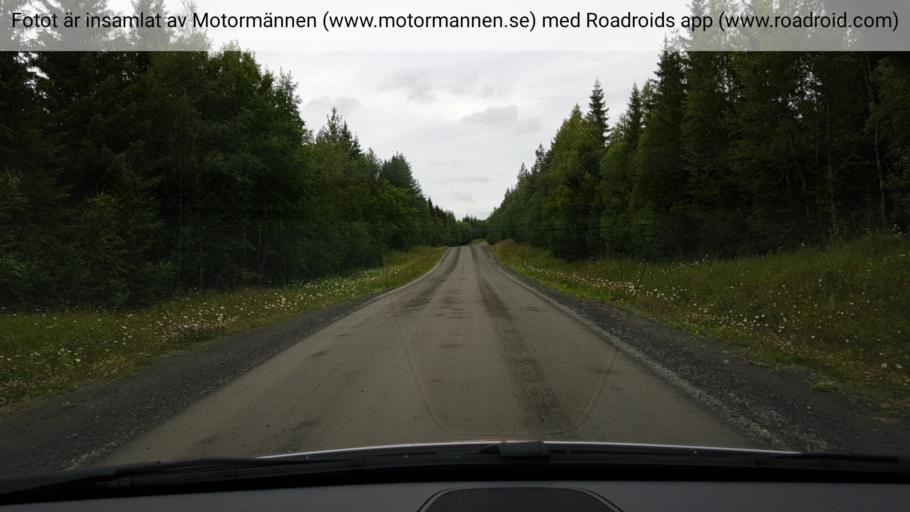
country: SE
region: Jaemtland
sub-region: Krokoms Kommun
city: Krokom
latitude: 63.7070
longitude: 14.5306
